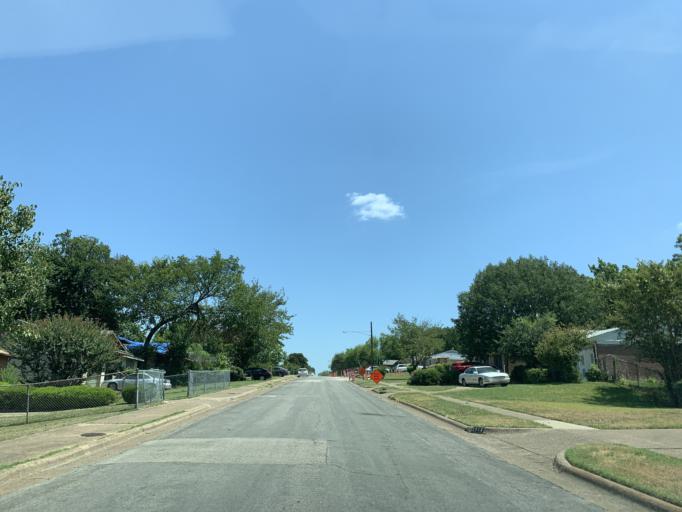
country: US
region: Texas
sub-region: Dallas County
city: Hutchins
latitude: 32.6811
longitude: -96.7652
